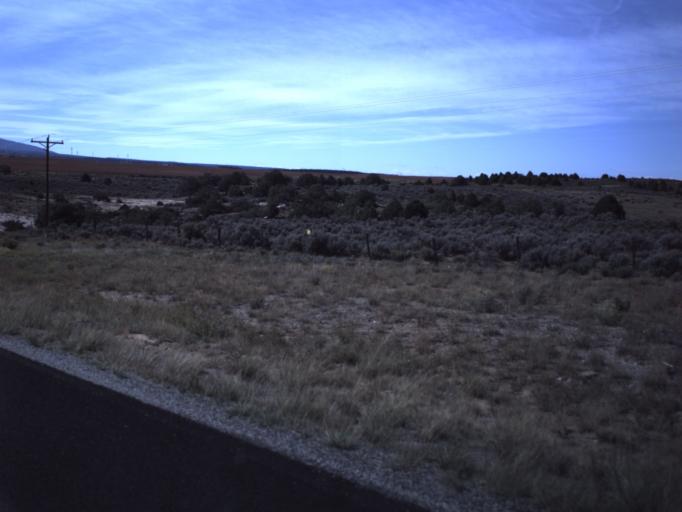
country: US
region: Utah
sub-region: San Juan County
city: Monticello
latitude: 37.8729
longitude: -109.2790
